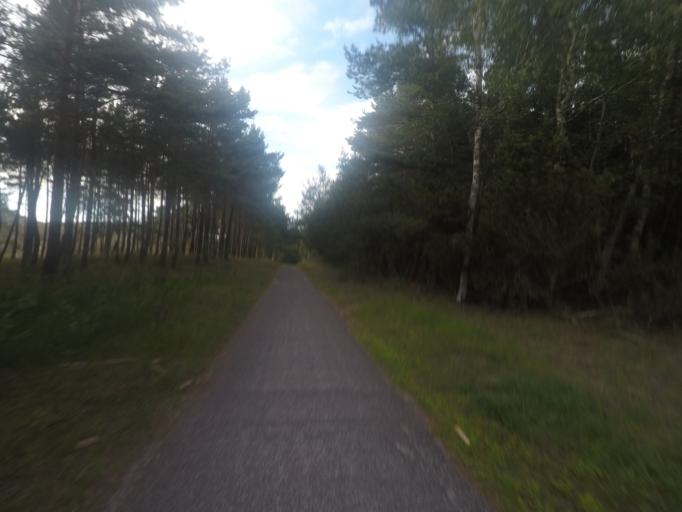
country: LT
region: Klaipedos apskritis
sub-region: Klaipeda
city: Klaipeda
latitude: 55.6470
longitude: 21.1081
